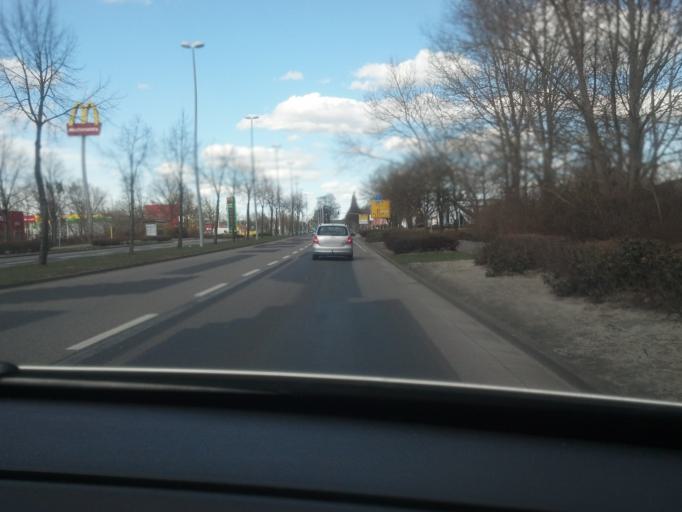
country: DE
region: Mecklenburg-Vorpommern
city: Neubrandenburg
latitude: 53.5835
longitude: 13.2716
